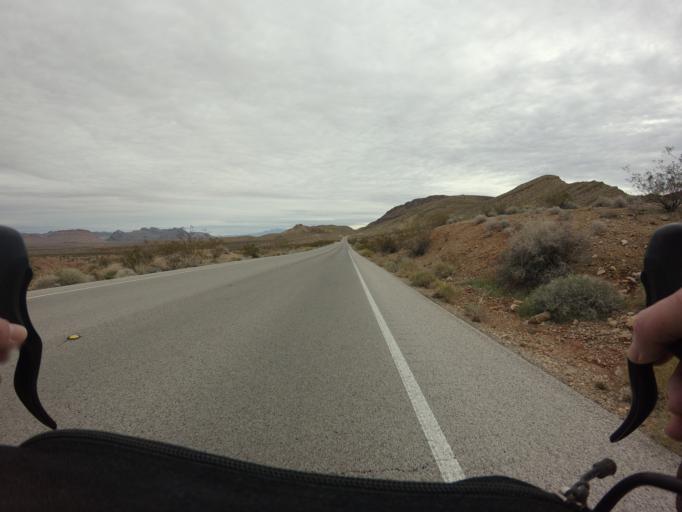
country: US
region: Nevada
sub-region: Clark County
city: Boulder City
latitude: 36.2288
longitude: -114.5794
